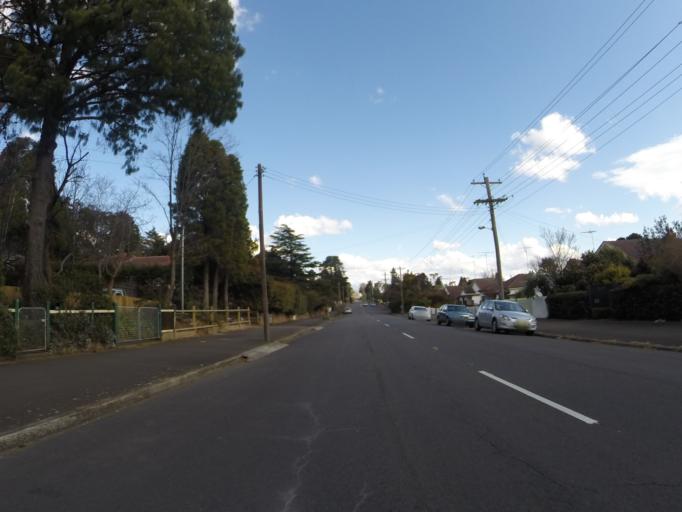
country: AU
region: New South Wales
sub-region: Blue Mountains Municipality
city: Katoomba
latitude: -33.7229
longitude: 150.3098
